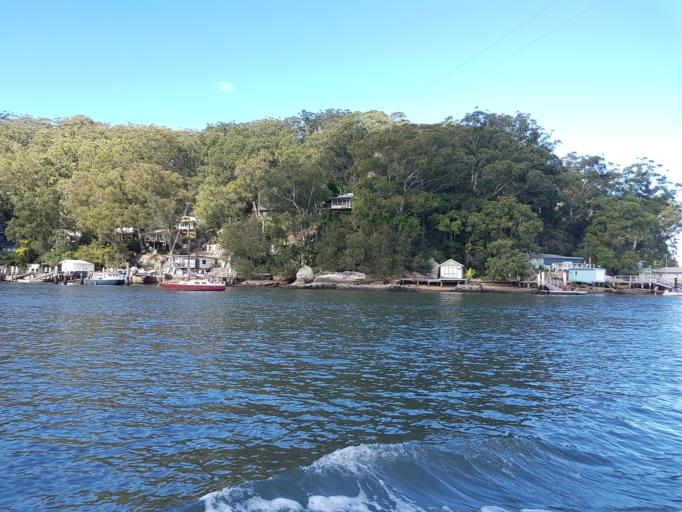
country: AU
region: New South Wales
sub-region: Gosford Shire
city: Umina
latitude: -33.5398
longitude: 151.2340
